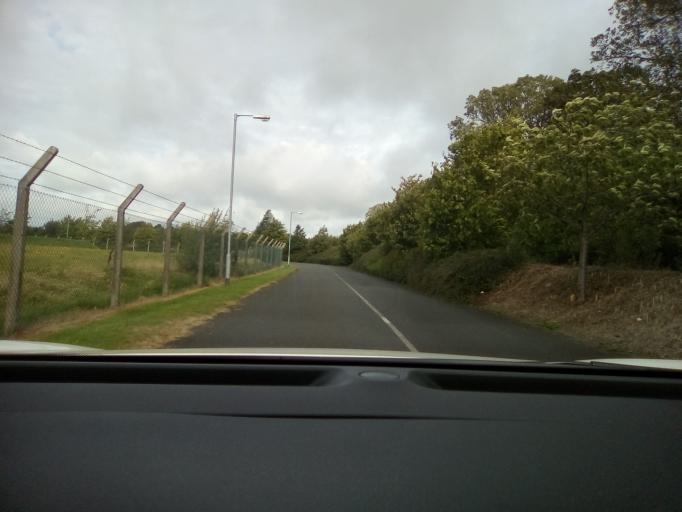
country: IE
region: Leinster
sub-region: Kildare
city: Leixlip
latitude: 53.3572
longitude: -6.4861
